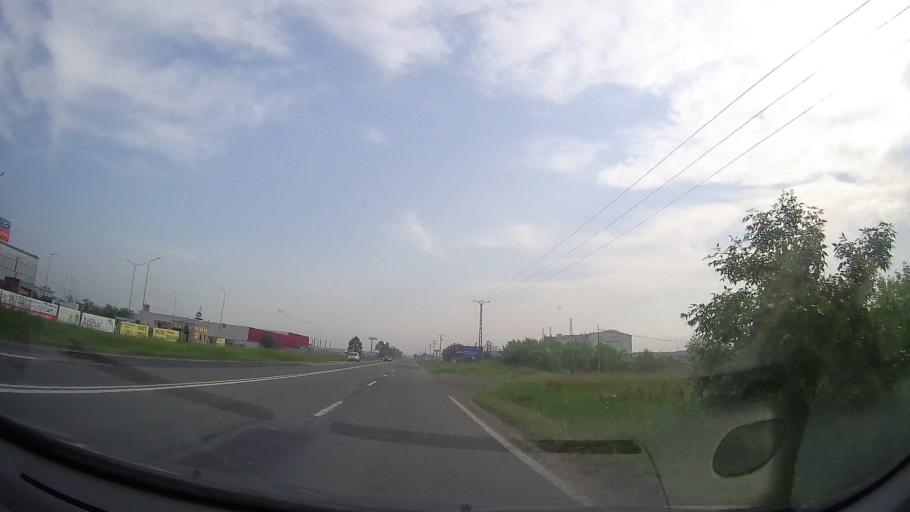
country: RO
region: Timis
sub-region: Comuna Giroc
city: Chisoda
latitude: 45.6951
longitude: 21.1778
